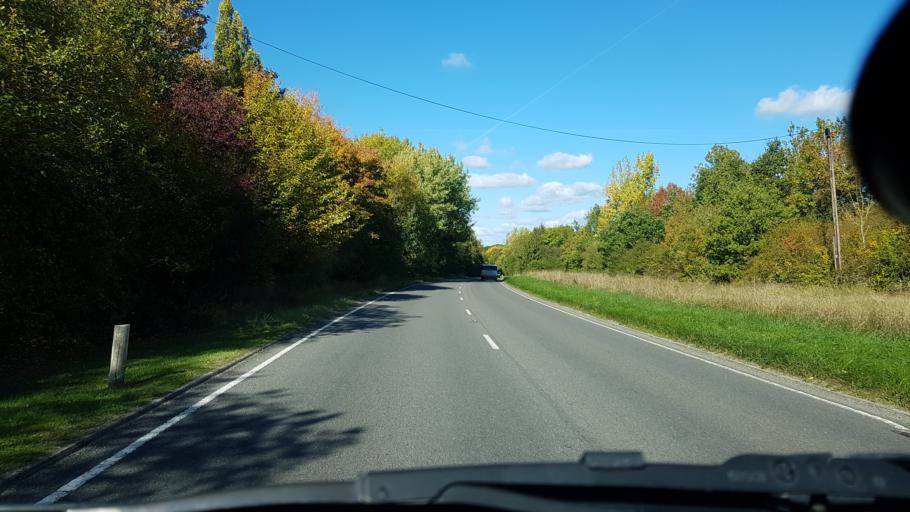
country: GB
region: England
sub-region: West Sussex
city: Billingshurst
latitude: 51.0085
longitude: -0.4316
